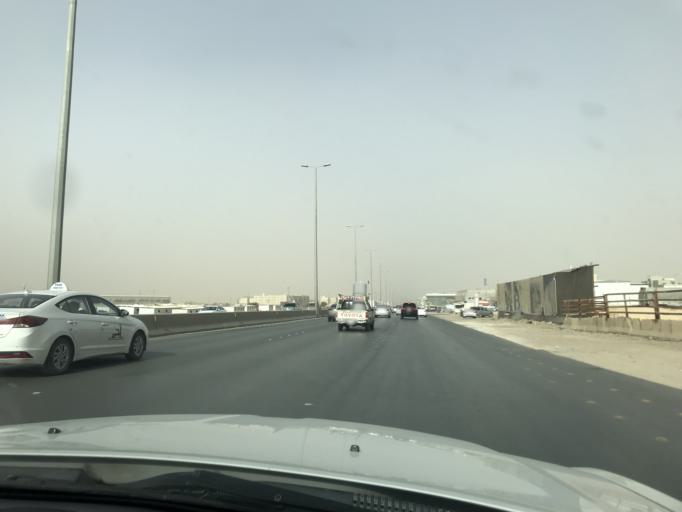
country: SA
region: Ar Riyad
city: Riyadh
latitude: 24.8298
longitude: 46.7270
